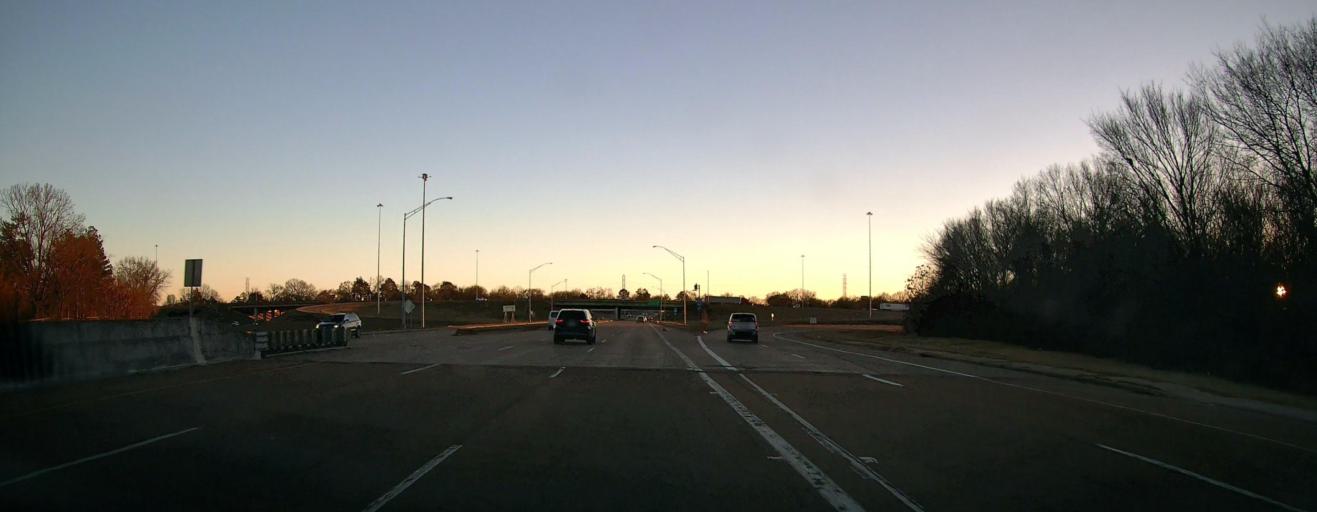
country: US
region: Tennessee
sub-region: Shelby County
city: Bartlett
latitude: 35.1962
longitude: -89.9256
